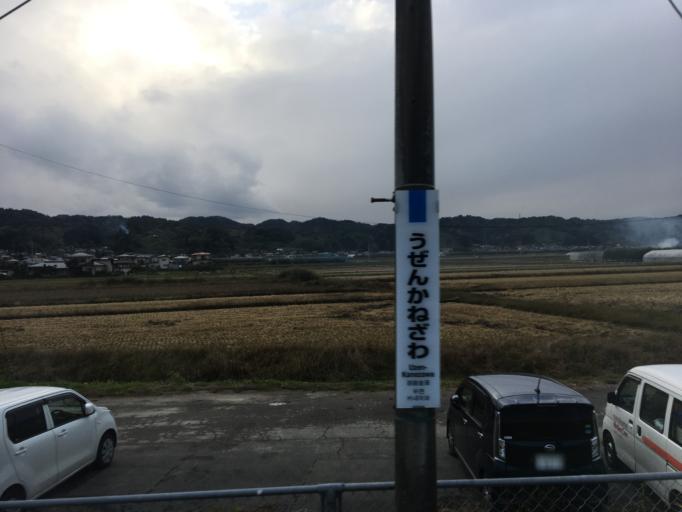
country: JP
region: Yamagata
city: Sagae
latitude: 38.3208
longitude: 140.2704
